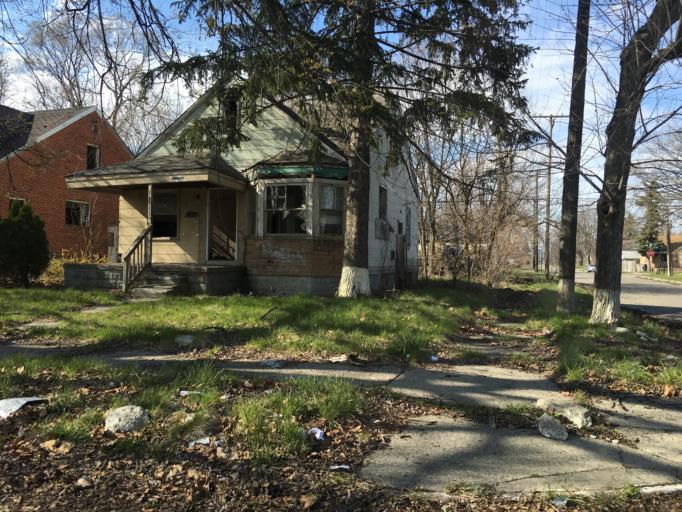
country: US
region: Michigan
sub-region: Macomb County
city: Eastpointe
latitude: 42.4264
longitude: -82.9678
